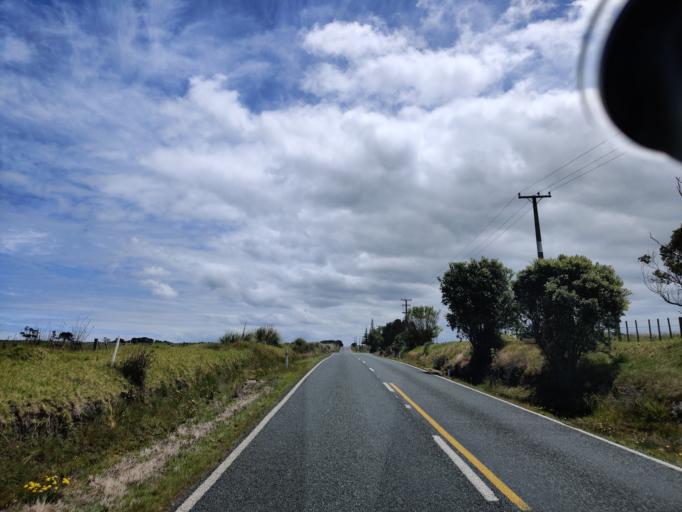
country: NZ
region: Northland
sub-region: Far North District
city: Kaitaia
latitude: -34.7035
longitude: 173.0299
